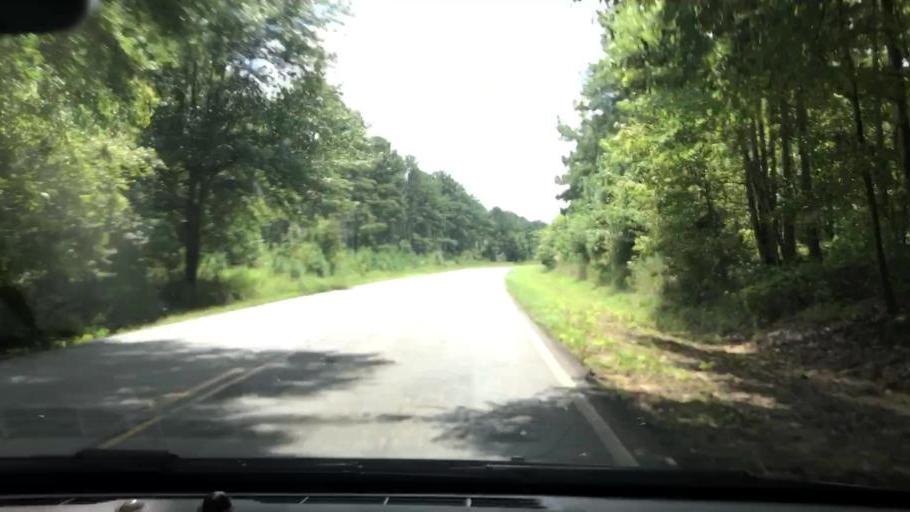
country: US
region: Georgia
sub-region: Quitman County
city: Georgetown
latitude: 32.0060
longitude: -85.0336
